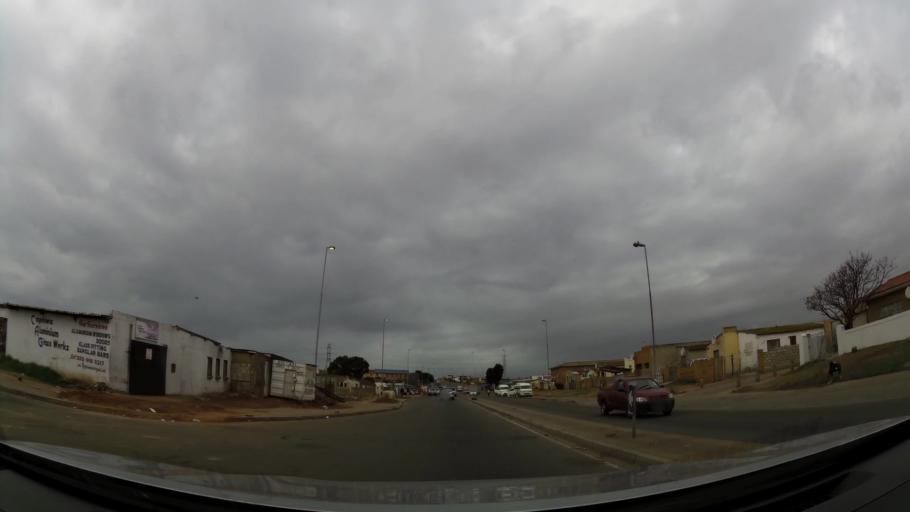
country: ZA
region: Eastern Cape
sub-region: Nelson Mandela Bay Metropolitan Municipality
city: Port Elizabeth
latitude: -33.8889
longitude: 25.5872
